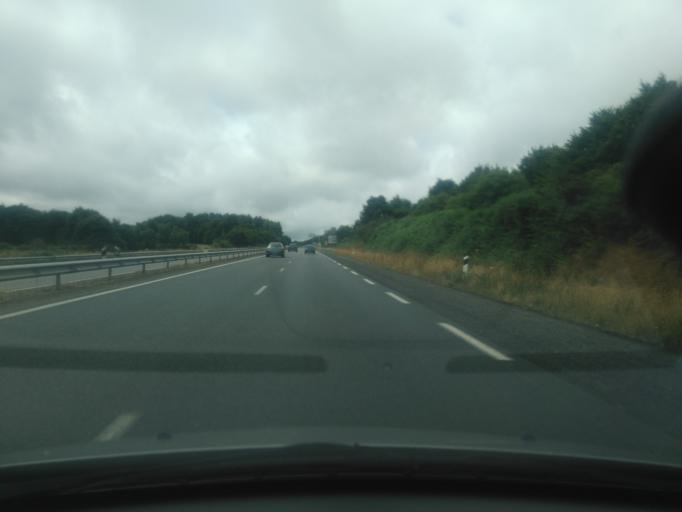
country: FR
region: Brittany
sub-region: Departement des Cotes-d'Armor
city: Saint-Julien
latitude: 48.4383
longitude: -2.8129
